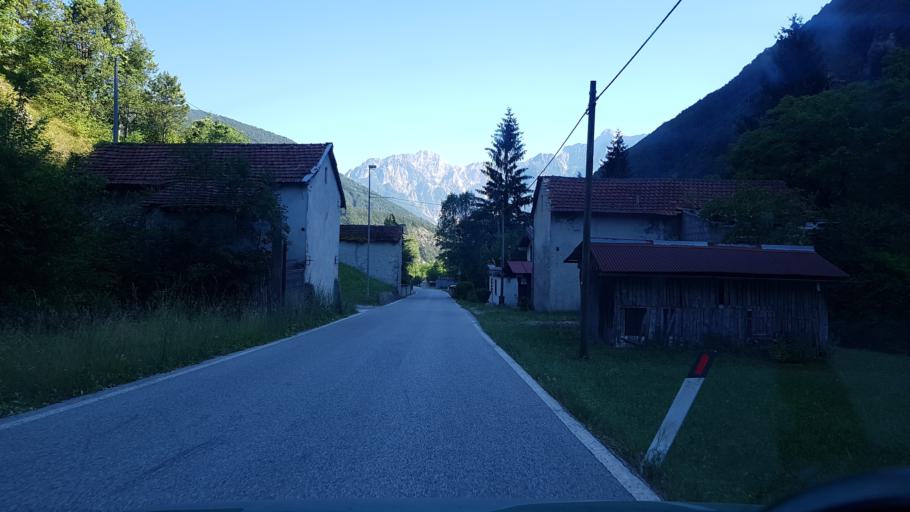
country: IT
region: Friuli Venezia Giulia
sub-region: Provincia di Udine
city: Moggio Udinese
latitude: 46.4339
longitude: 13.1989
